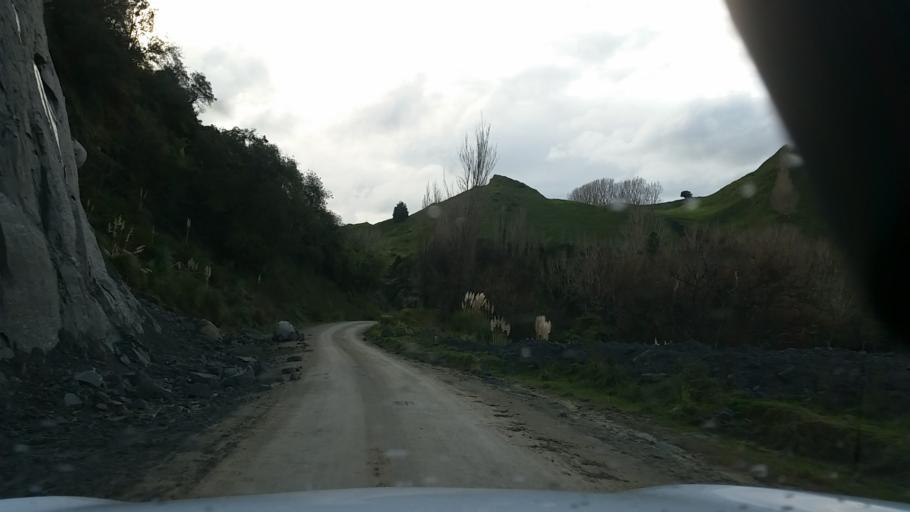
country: NZ
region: Taranaki
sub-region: South Taranaki District
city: Patea
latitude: -39.5583
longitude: 174.8062
